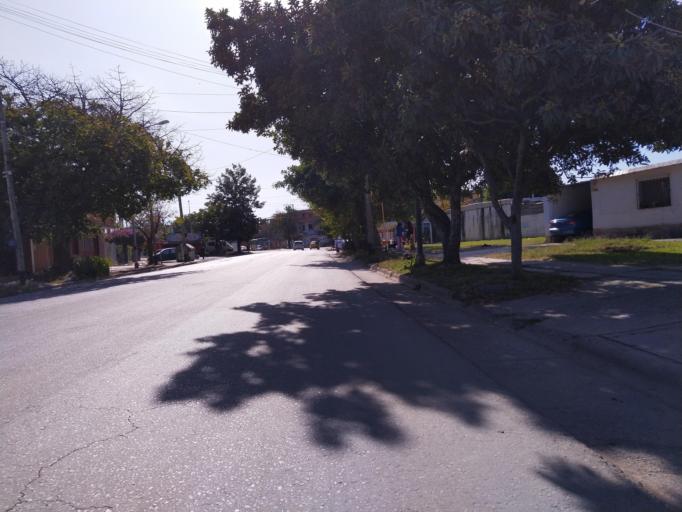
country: AR
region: Jujuy
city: San Salvador de Jujuy
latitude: -24.1994
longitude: -65.2794
